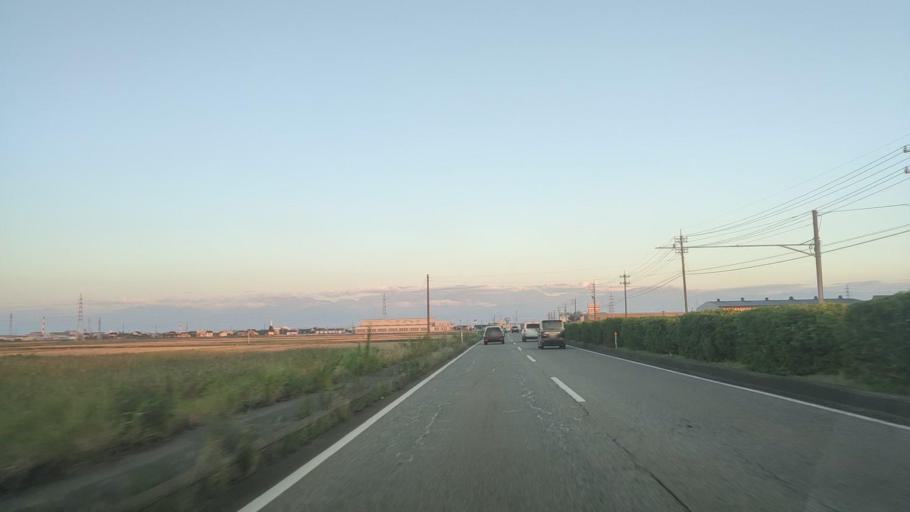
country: JP
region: Toyama
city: Nishishinminato
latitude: 36.7480
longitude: 137.0954
